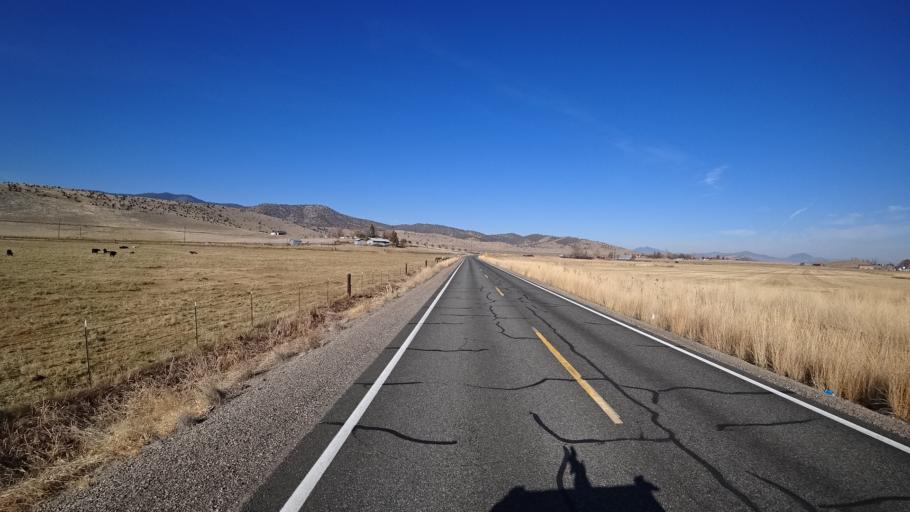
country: US
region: California
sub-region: Siskiyou County
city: Montague
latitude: 41.6062
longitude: -122.5269
